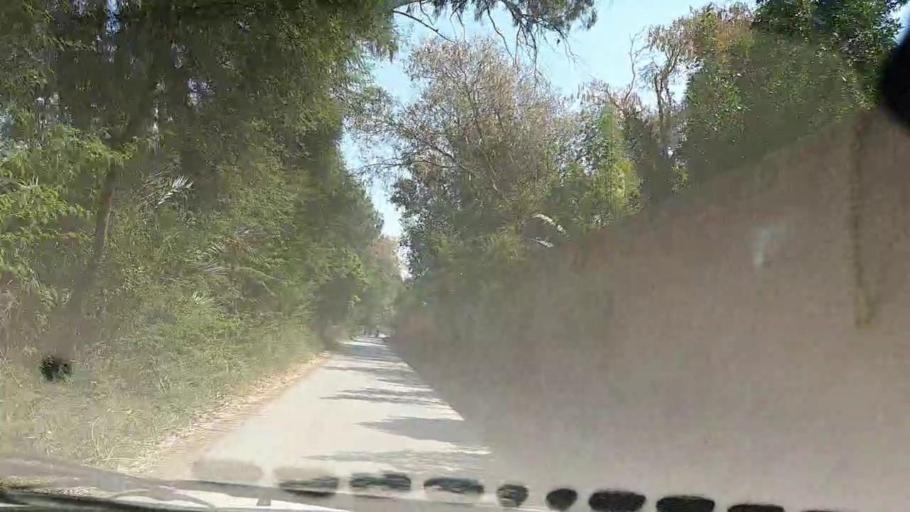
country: PK
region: Sindh
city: Mirpur Khas
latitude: 25.4718
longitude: 69.0289
